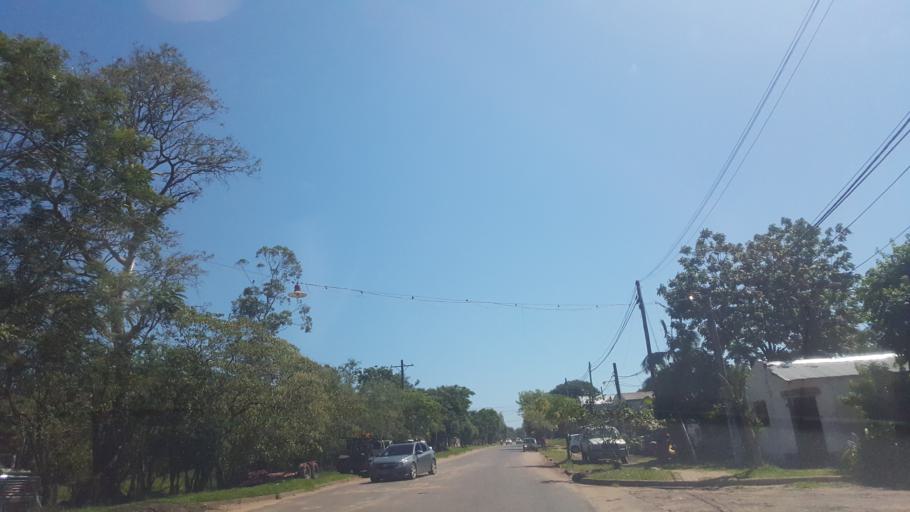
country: AR
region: Corrientes
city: Ituzaingo
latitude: -27.5923
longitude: -56.6930
